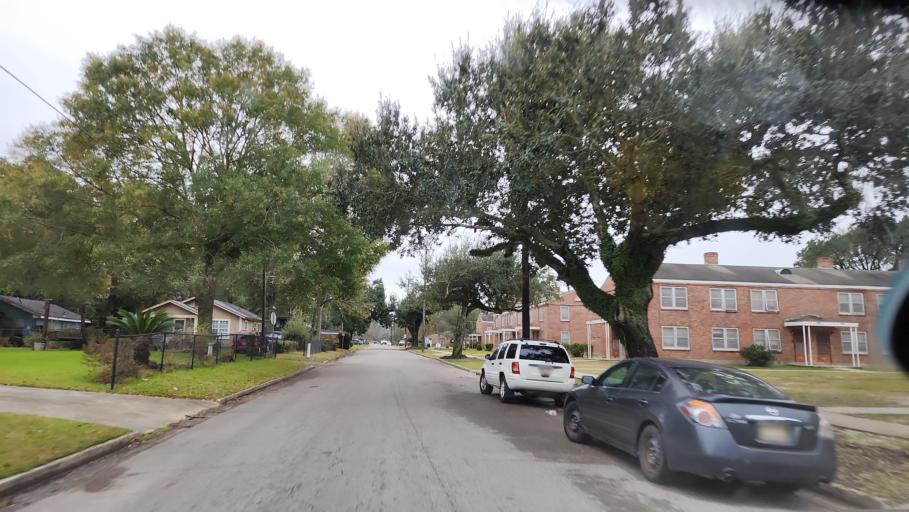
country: US
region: Mississippi
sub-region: Forrest County
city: Hattiesburg
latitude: 31.3149
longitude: -89.2947
